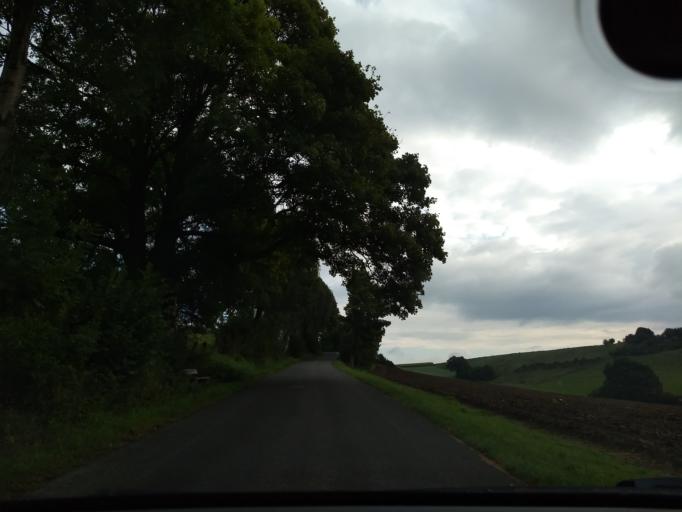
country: DE
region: North Rhine-Westphalia
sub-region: Regierungsbezirk Detmold
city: Buren
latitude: 51.5262
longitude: 8.5395
